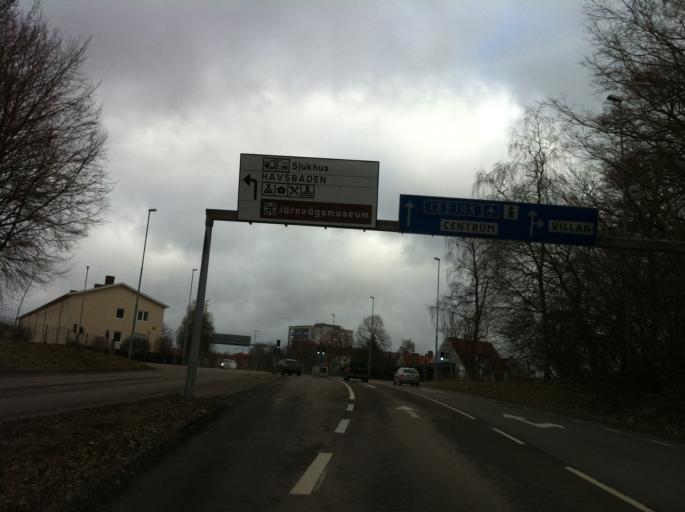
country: SE
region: Skane
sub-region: Angelholms Kommun
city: AEngelholm
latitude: 56.2339
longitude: 12.8608
